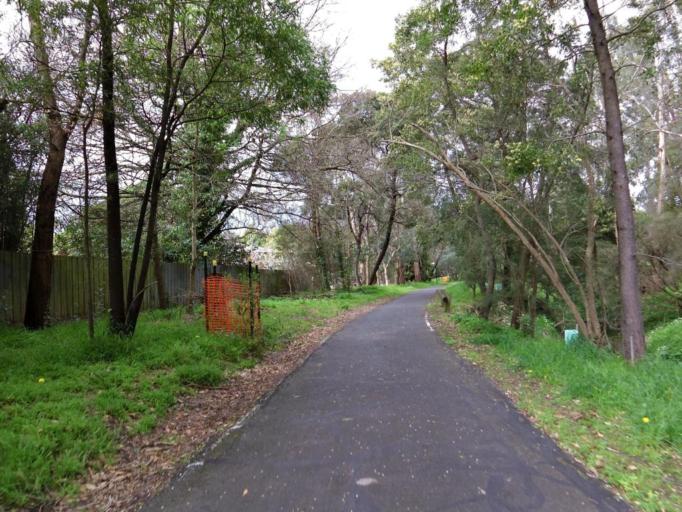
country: AU
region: Victoria
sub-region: Maroondah
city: Warranwood
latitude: -37.7954
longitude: 145.2525
